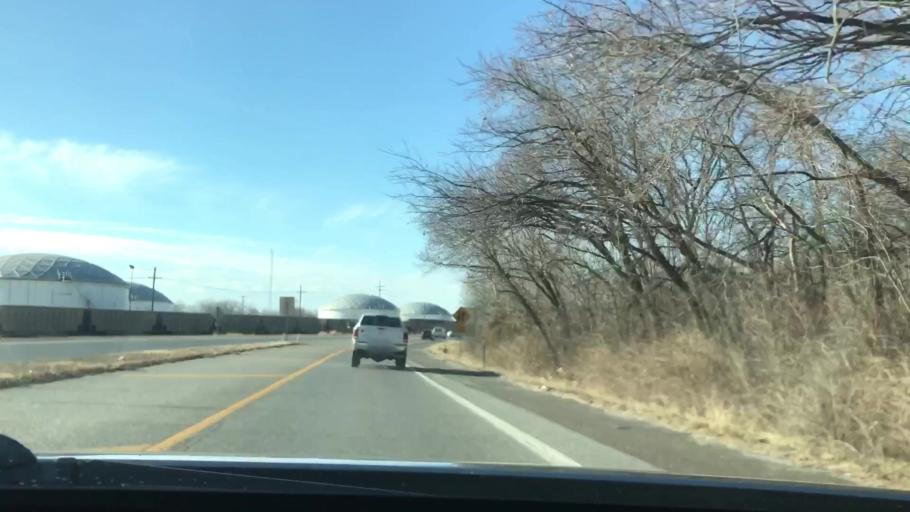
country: US
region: Missouri
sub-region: Platte County
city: Parkville
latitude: 39.1794
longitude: -94.6558
